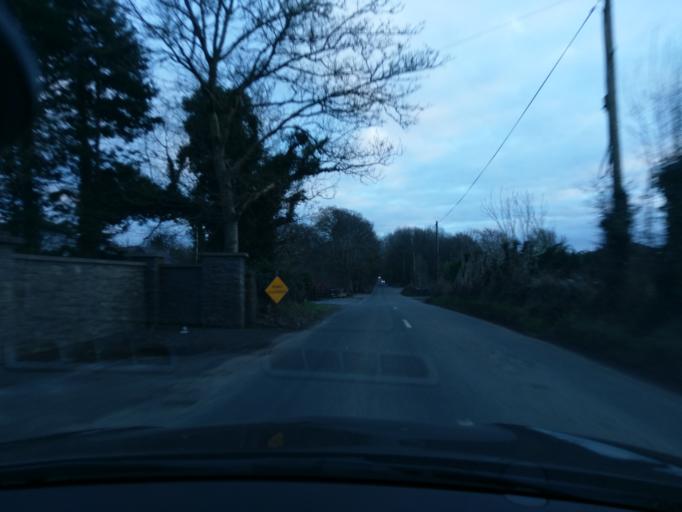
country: IE
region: Connaught
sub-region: County Galway
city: Athenry
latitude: 53.3399
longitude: -8.7737
